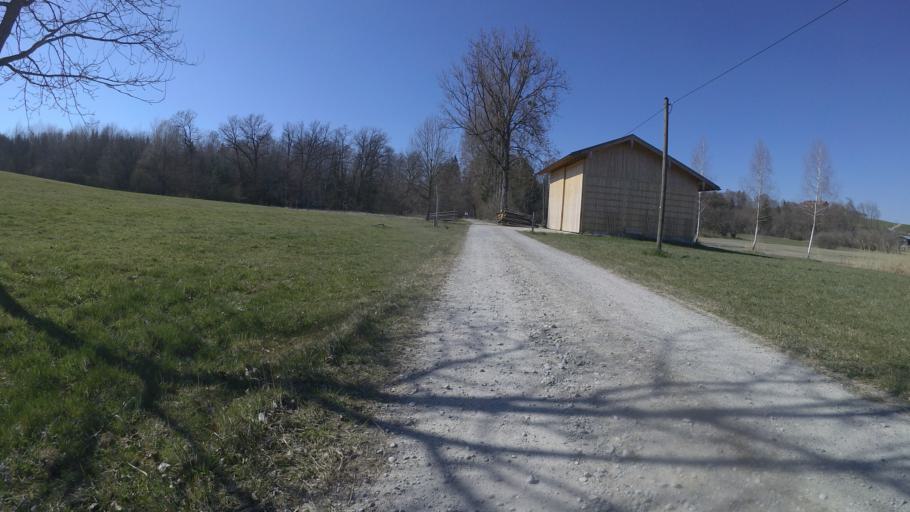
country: DE
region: Bavaria
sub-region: Upper Bavaria
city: Seeon-Seebruck
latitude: 47.9642
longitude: 12.4899
